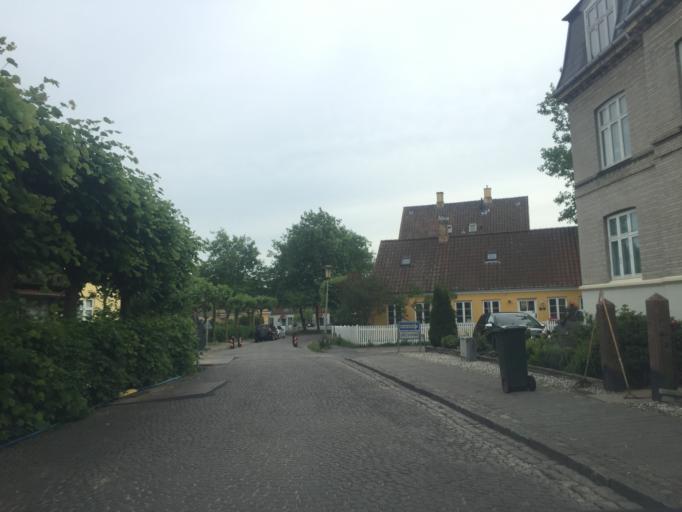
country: DK
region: Capital Region
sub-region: Lyngby-Tarbaek Kommune
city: Kongens Lyngby
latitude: 55.7774
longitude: 12.5045
